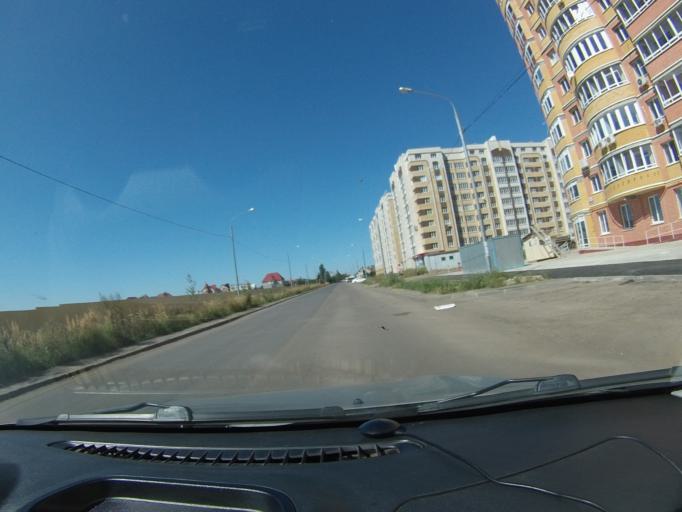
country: RU
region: Tambov
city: Tambov
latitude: 52.7710
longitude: 41.3936
